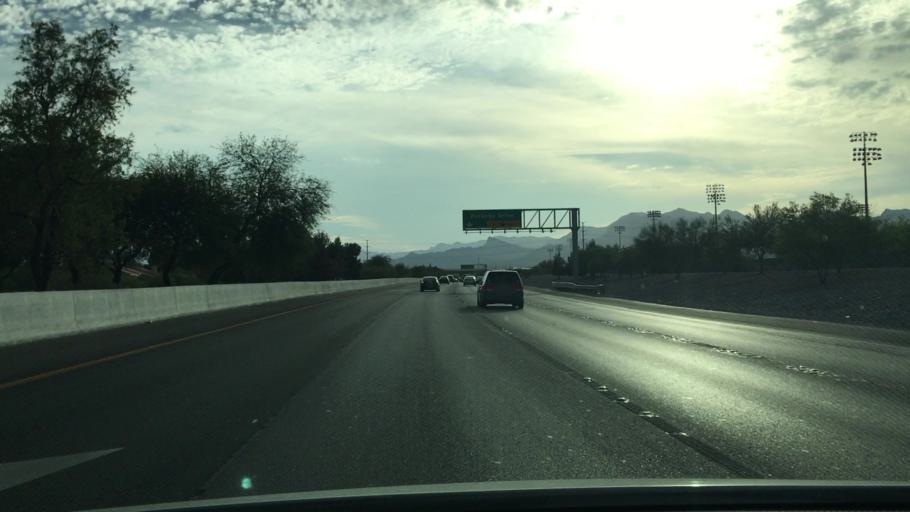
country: US
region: Nevada
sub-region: Clark County
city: Spring Valley
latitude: 36.1783
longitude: -115.2659
